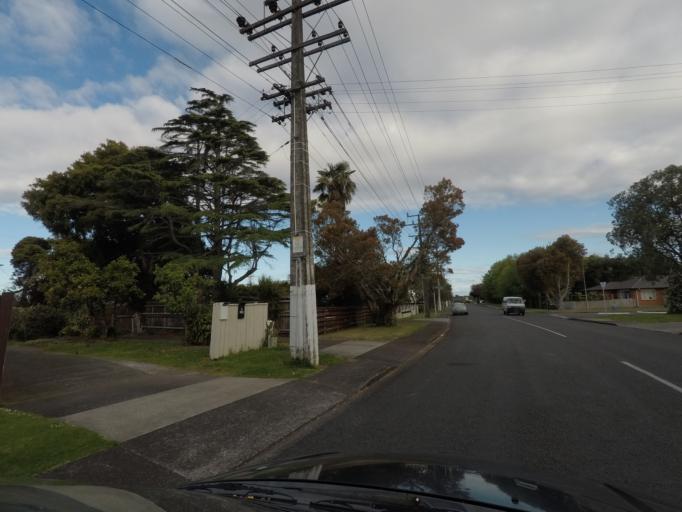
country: NZ
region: Auckland
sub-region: Auckland
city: Rosebank
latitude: -36.8849
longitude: 174.6584
